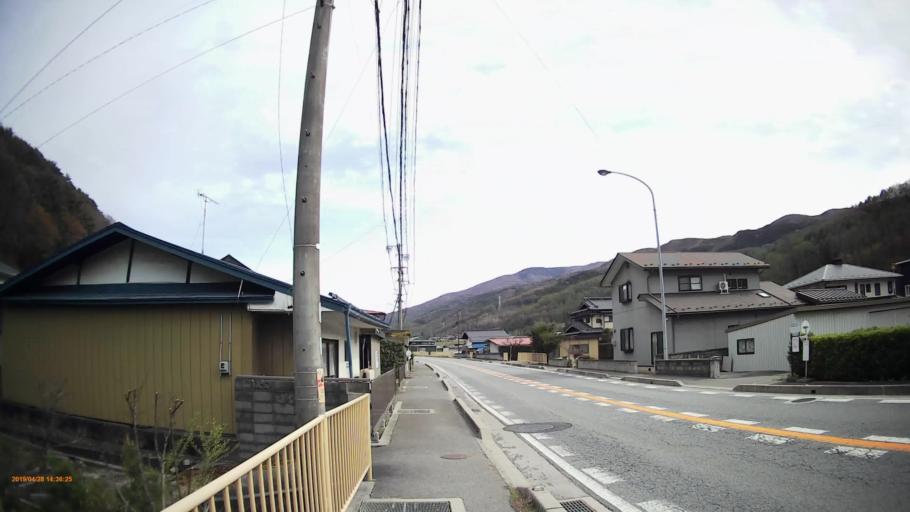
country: JP
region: Nagano
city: Chino
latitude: 35.9658
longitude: 138.1752
